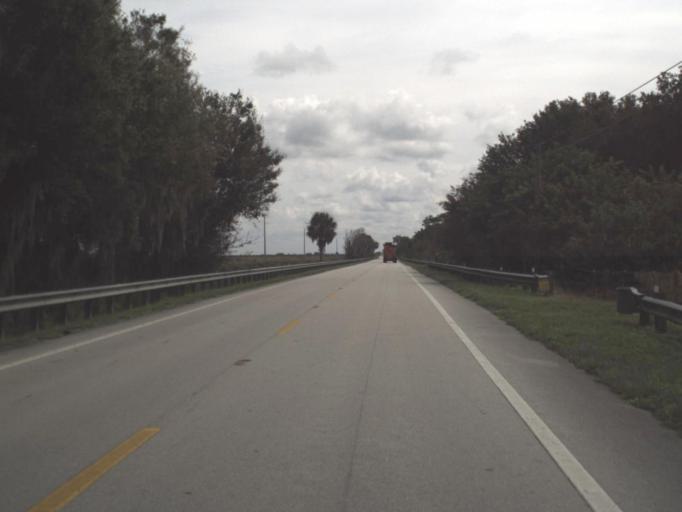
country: US
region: Florida
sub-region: Highlands County
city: Lake Placid
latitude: 27.2084
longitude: -81.2721
